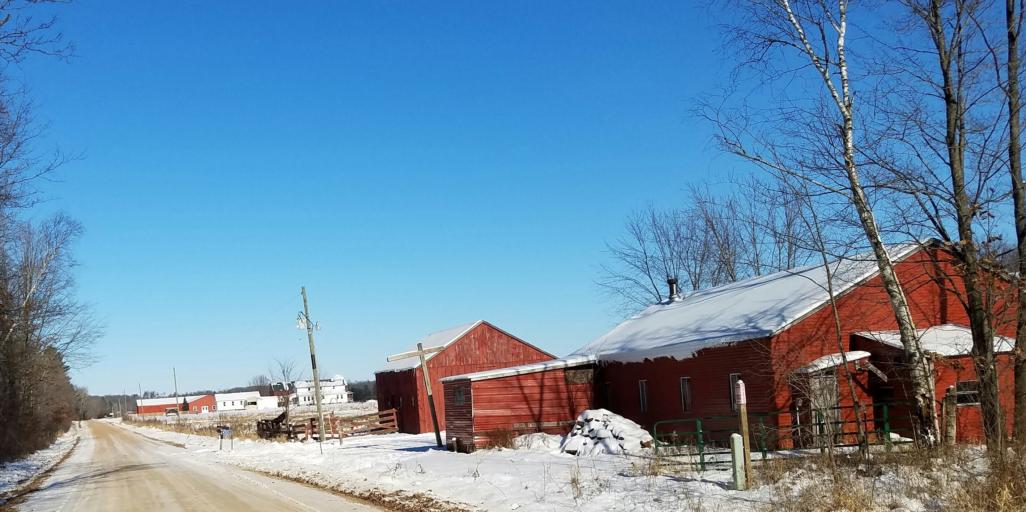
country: US
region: Wisconsin
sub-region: Marathon County
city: Spencer
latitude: 44.5611
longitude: -90.3761
